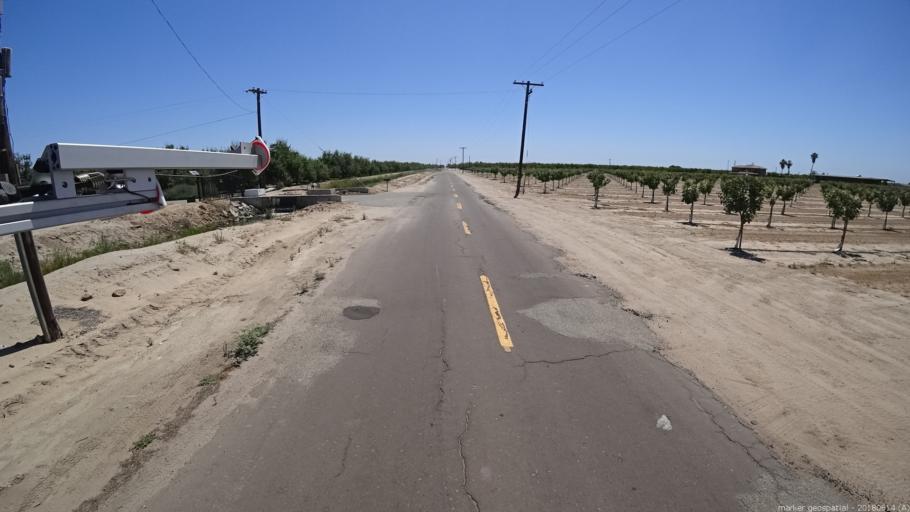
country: US
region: California
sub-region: Madera County
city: Fairmead
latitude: 36.9892
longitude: -120.2342
